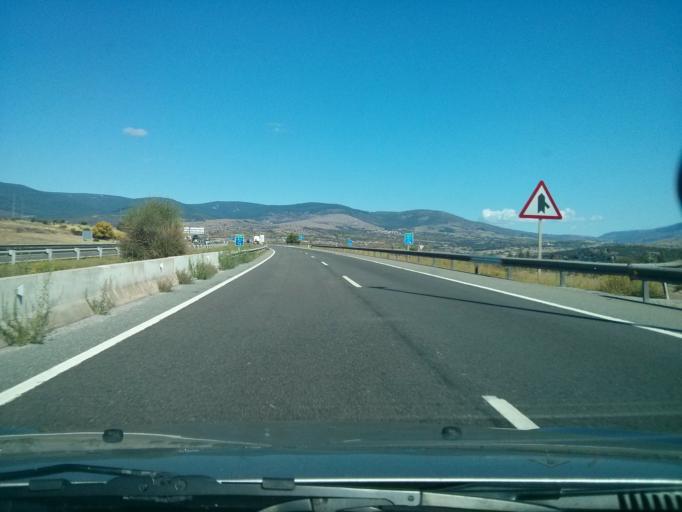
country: ES
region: Madrid
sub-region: Provincia de Madrid
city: Buitrago del Lozoya
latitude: 40.9812
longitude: -3.6387
